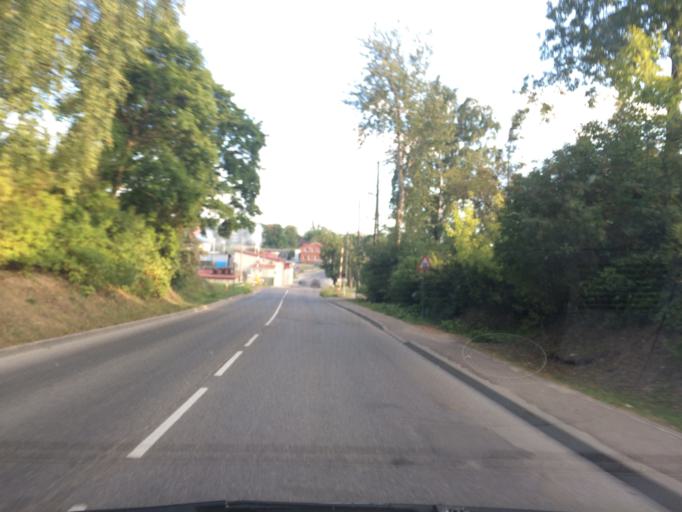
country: LV
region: Rezekne
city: Rezekne
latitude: 56.5149
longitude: 27.3229
